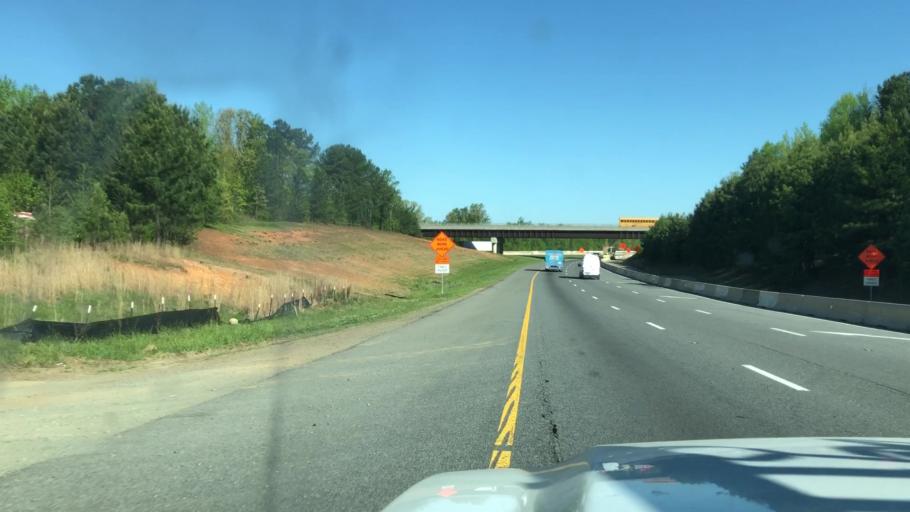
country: US
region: North Carolina
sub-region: Mecklenburg County
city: Huntersville
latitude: 35.3669
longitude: -80.8406
